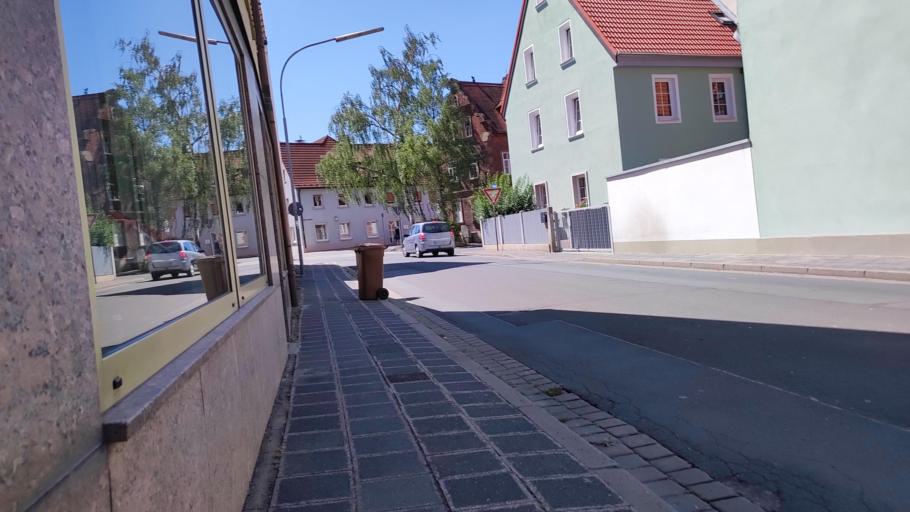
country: DE
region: Bavaria
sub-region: Regierungsbezirk Mittelfranken
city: Neustadt an der Aisch
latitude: 49.5778
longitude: 10.6015
